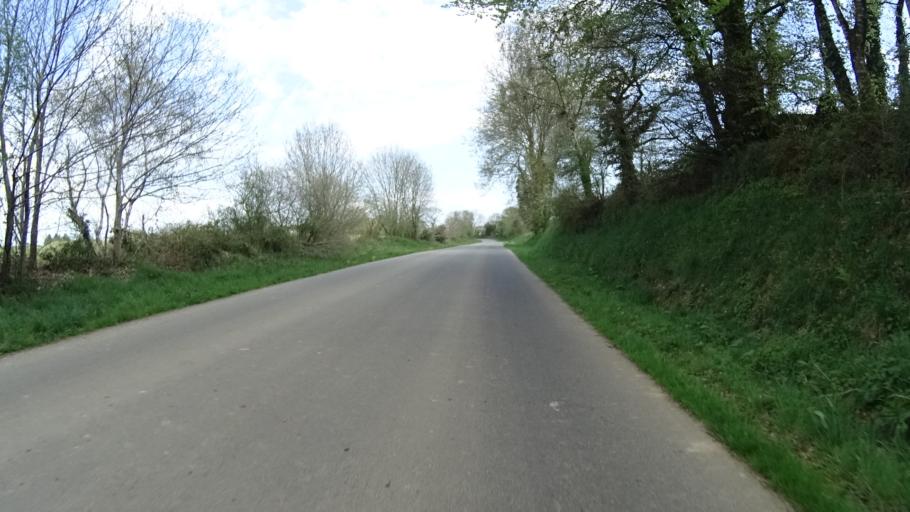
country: FR
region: Brittany
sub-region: Departement du Finistere
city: Sizun
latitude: 48.4281
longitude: -4.0570
